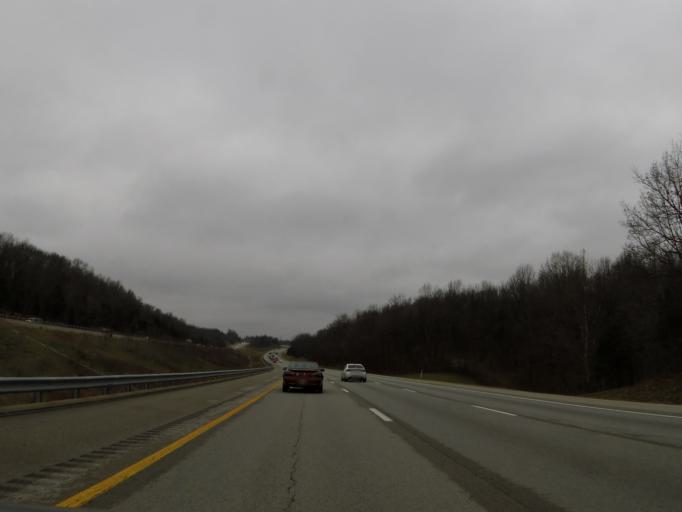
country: US
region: Kentucky
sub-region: Grant County
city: Williamstown
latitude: 38.4248
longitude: -84.5768
